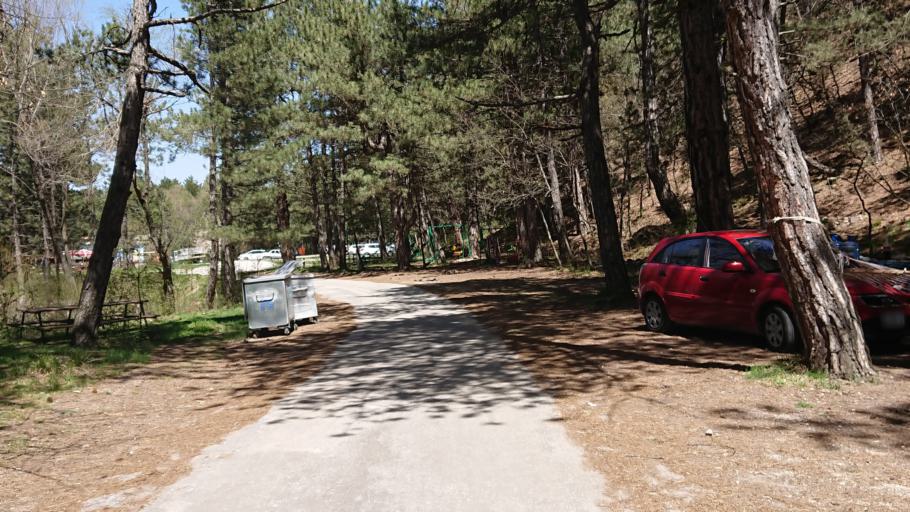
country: TR
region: Kuetahya
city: Sabuncu
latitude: 39.5127
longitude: 30.4238
